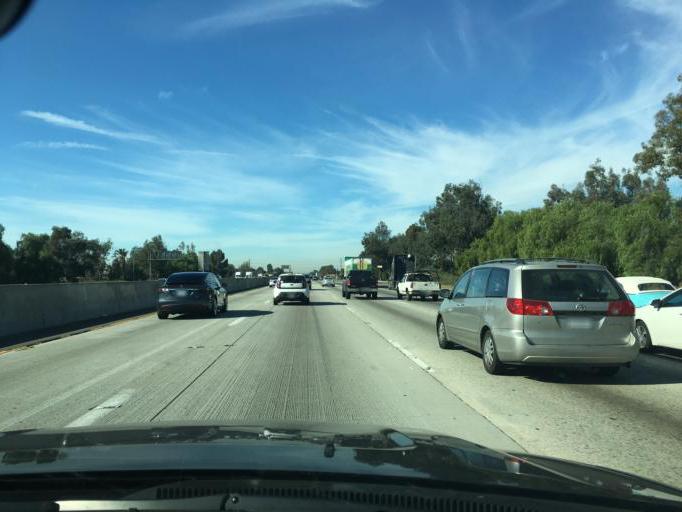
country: US
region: California
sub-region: San Bernardino County
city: Ontario
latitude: 34.0306
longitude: -117.6089
